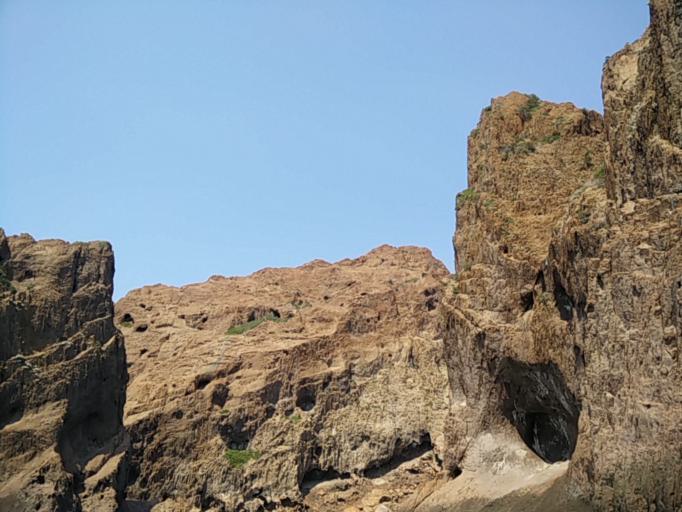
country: FR
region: Corsica
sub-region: Departement de la Corse-du-Sud
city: Cargese
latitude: 42.3443
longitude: 8.5526
